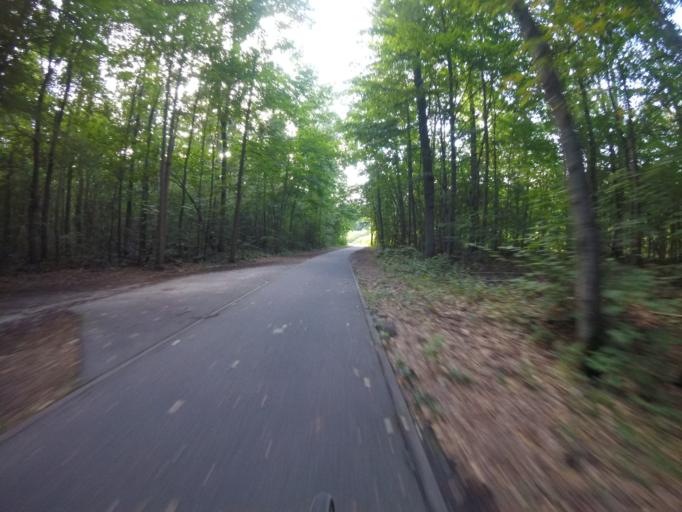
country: DE
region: Brandenburg
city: Petershagen
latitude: 52.5562
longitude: 13.7839
